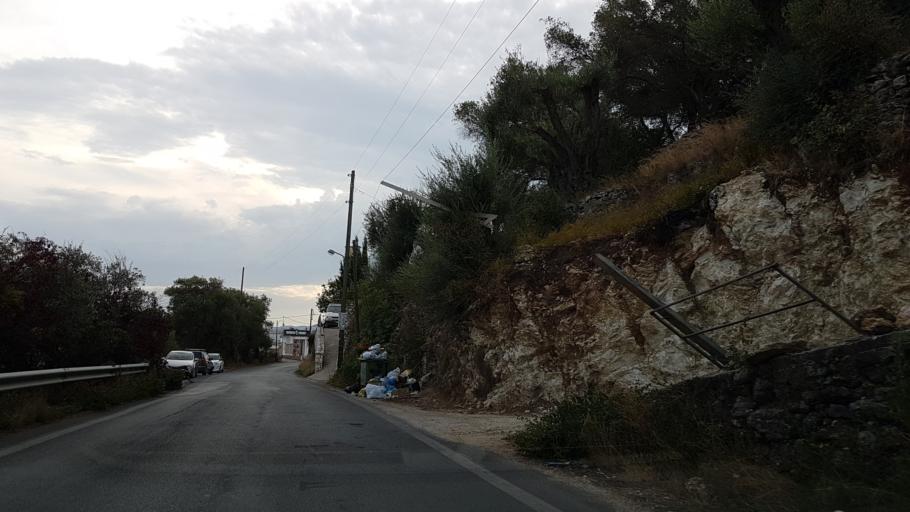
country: GR
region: Ionian Islands
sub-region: Nomos Kerkyras
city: Kontokali
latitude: 39.7274
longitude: 19.9063
